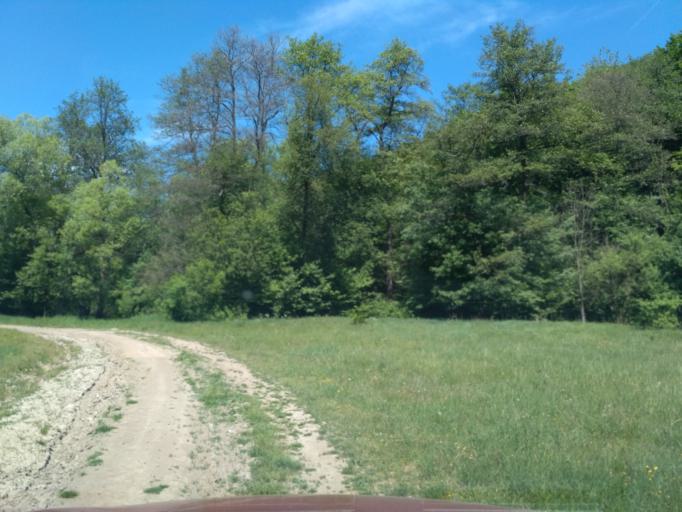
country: SK
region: Presovsky
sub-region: Okres Presov
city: Presov
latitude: 48.8843
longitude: 21.3953
